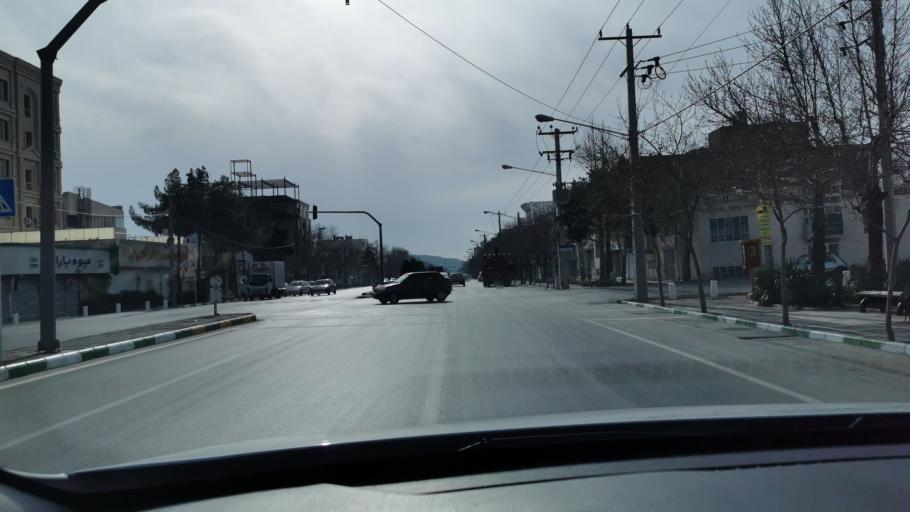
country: IR
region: Razavi Khorasan
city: Mashhad
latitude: 36.2893
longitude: 59.5405
